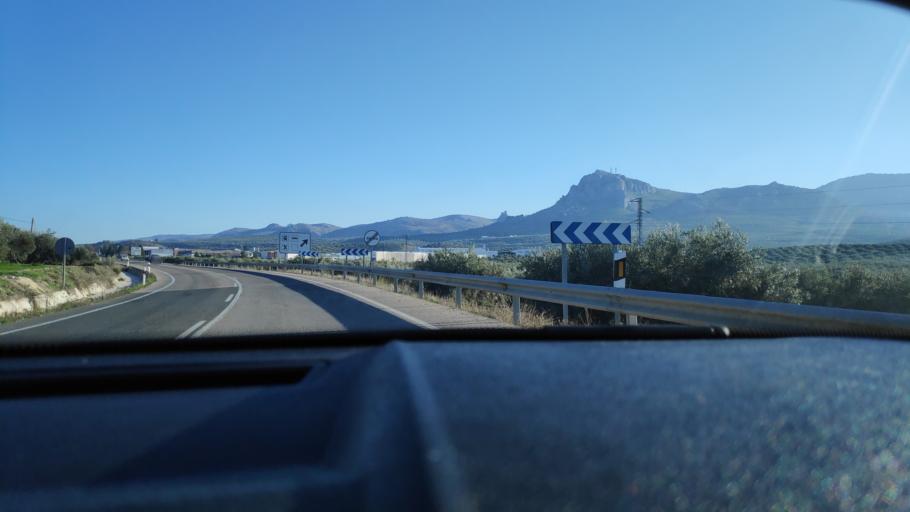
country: ES
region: Andalusia
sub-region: Province of Cordoba
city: Luque
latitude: 37.5843
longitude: -4.2901
